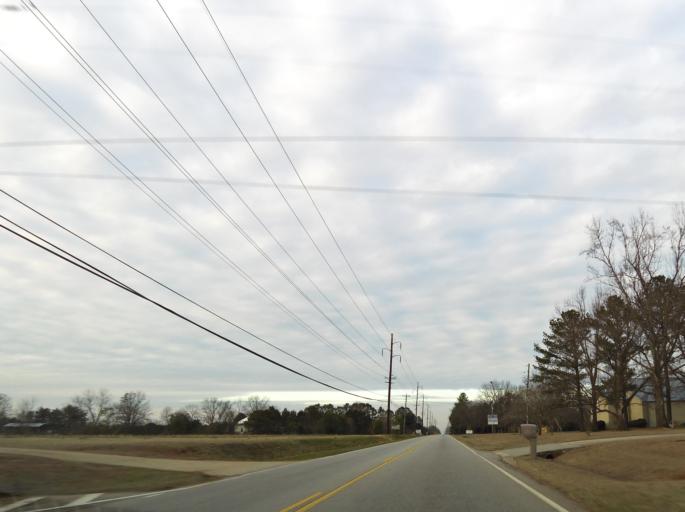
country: US
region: Georgia
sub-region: Houston County
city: Centerville
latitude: 32.6380
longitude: -83.7089
